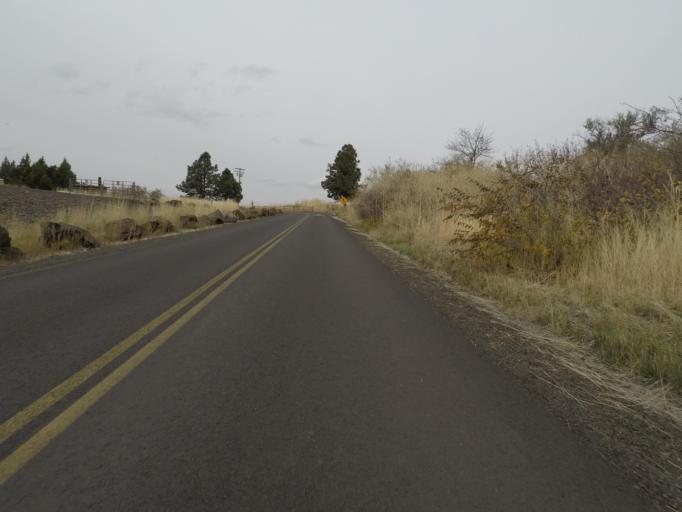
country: US
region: Washington
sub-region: Walla Walla County
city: Walla Walla East
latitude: 46.0669
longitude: -118.2663
